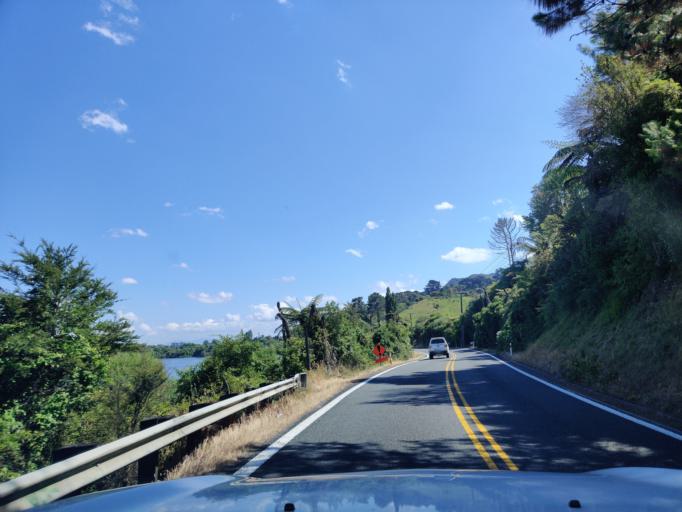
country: NZ
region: Waikato
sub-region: Waikato District
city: Ngaruawahia
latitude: -37.6525
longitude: 175.1439
